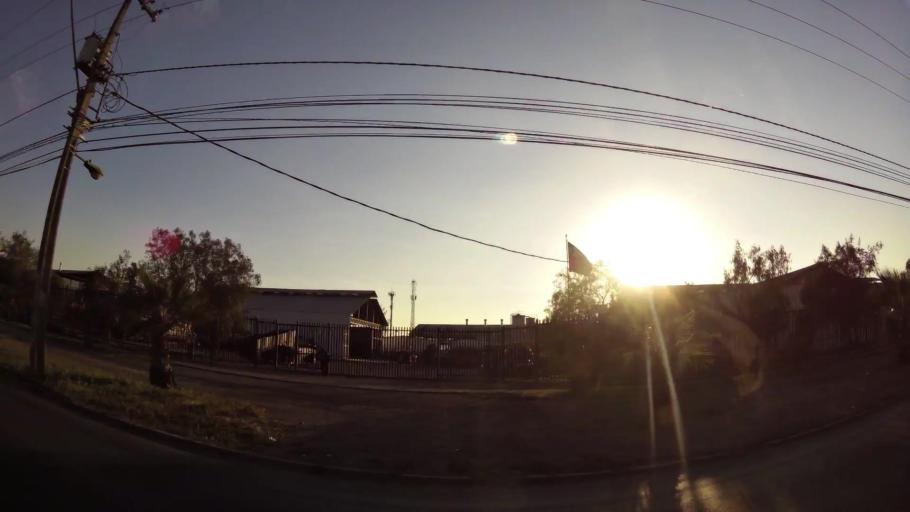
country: CL
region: Santiago Metropolitan
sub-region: Provincia de Santiago
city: La Pintana
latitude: -33.5250
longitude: -70.6251
